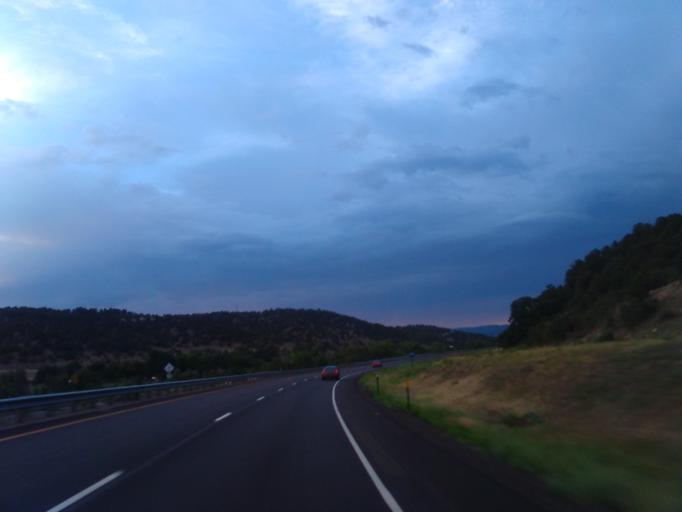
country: US
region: Colorado
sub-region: Las Animas County
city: Trinidad
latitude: 37.1032
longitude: -104.5240
